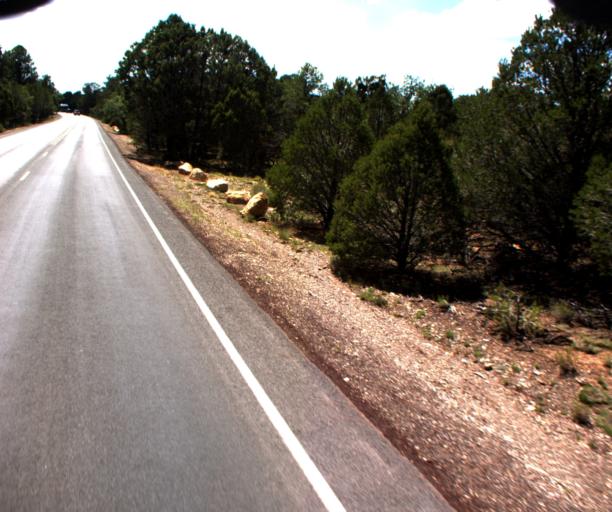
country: US
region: Arizona
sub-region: Coconino County
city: Grand Canyon
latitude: 36.0477
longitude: -112.1133
